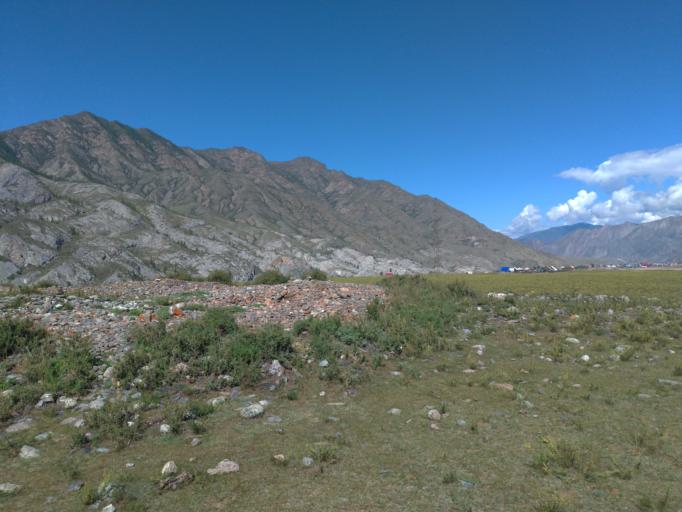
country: RU
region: Altay
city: Inya
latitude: 50.4340
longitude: 86.6222
